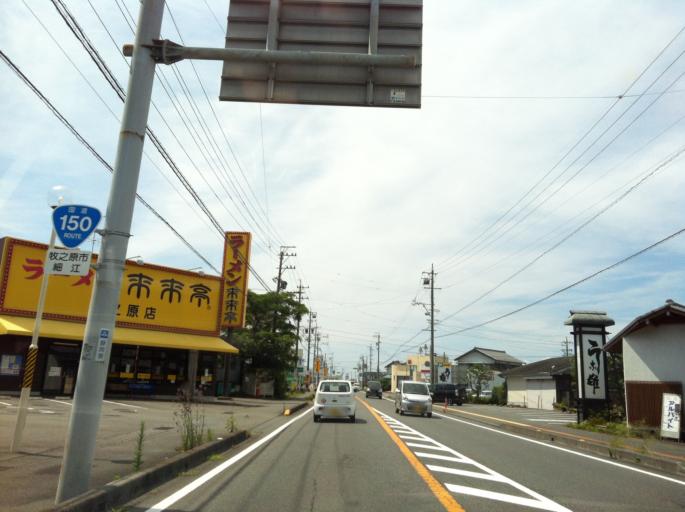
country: JP
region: Shizuoka
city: Sagara
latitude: 34.7473
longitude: 138.2378
